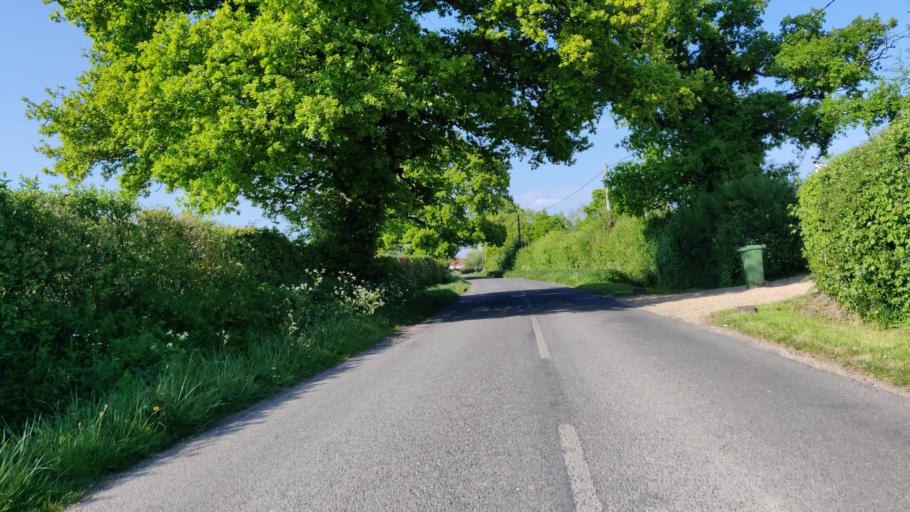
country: GB
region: England
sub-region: West Sussex
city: Southwater
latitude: 51.0382
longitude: -0.3583
